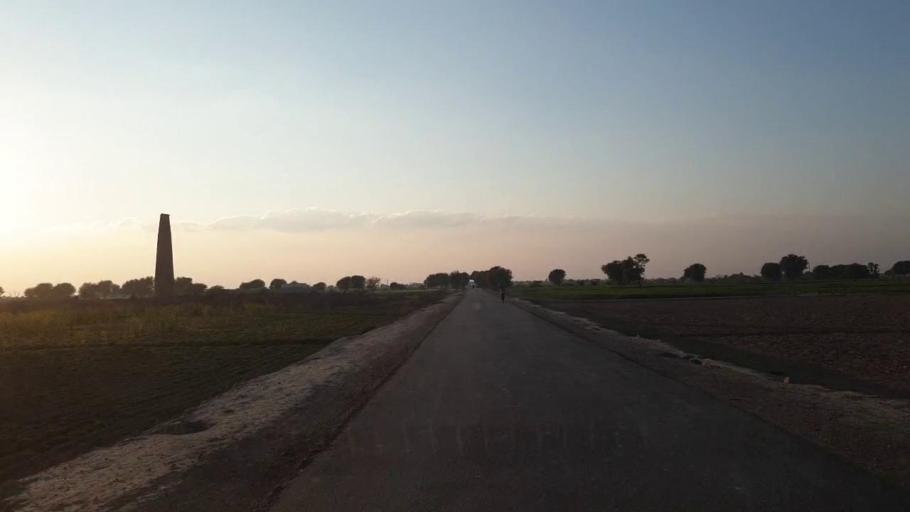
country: PK
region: Sindh
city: Shahpur Chakar
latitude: 26.1559
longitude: 68.5570
